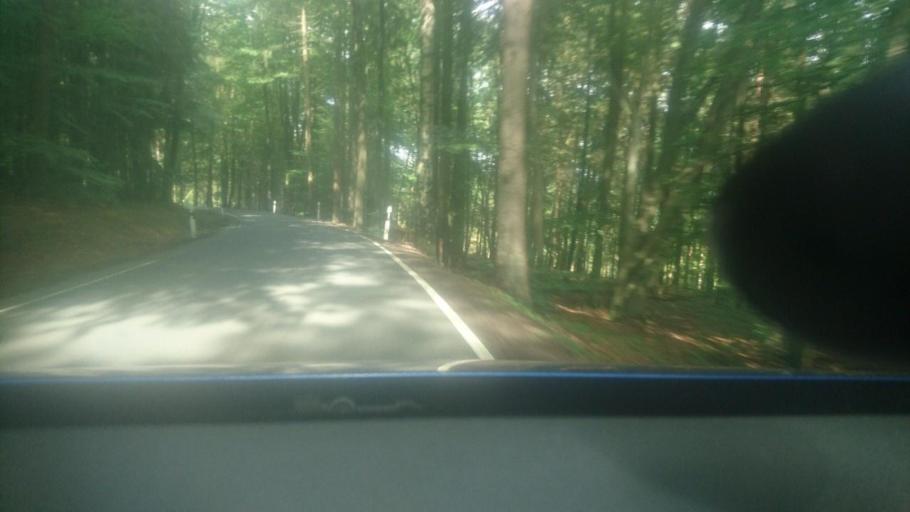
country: DE
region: Hesse
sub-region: Regierungsbezirk Darmstadt
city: Frankisch-Crumbach
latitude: 49.7069
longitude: 8.9237
